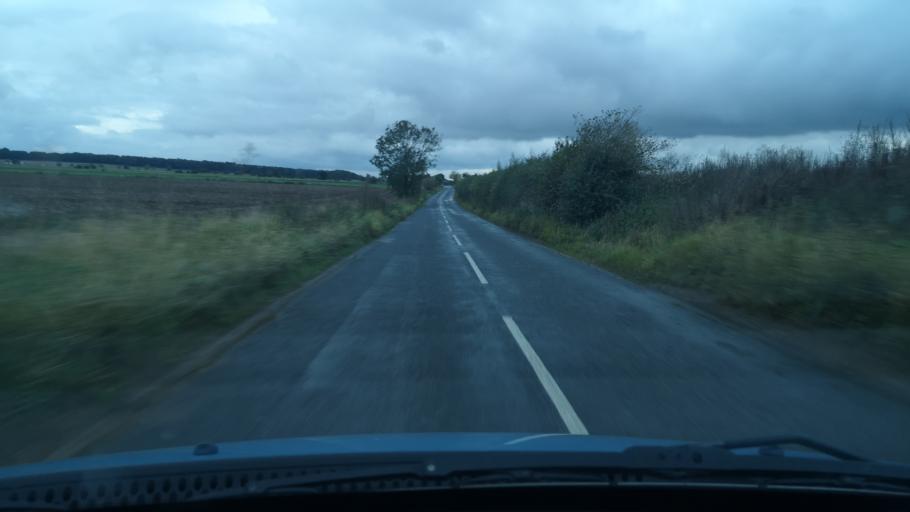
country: GB
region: England
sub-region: City and Borough of Wakefield
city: Darrington
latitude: 53.6459
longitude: -1.2427
